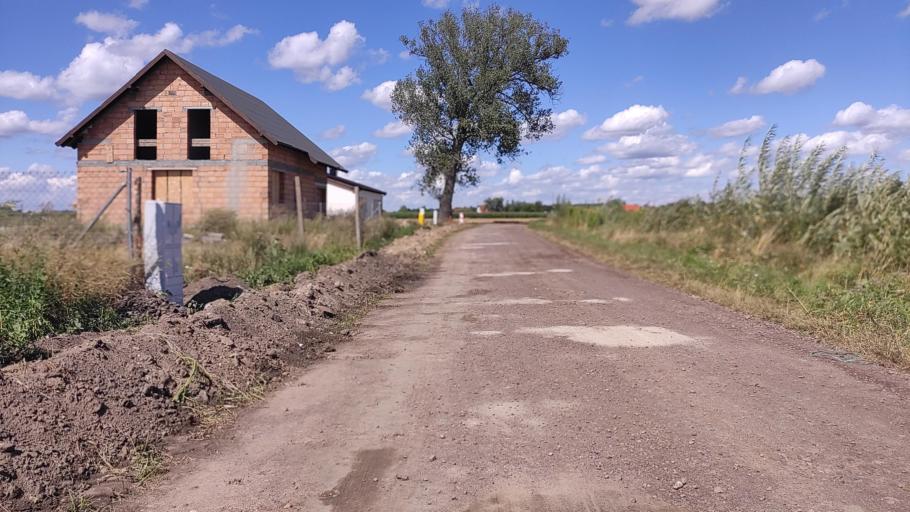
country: PL
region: Greater Poland Voivodeship
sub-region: Powiat poznanski
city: Kleszczewo
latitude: 52.3868
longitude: 17.1501
